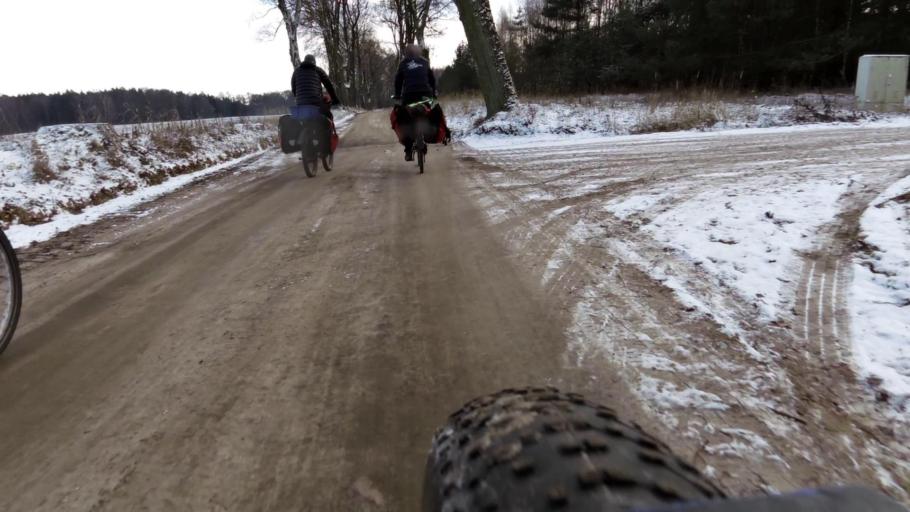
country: PL
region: West Pomeranian Voivodeship
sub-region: Powiat walecki
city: Walcz
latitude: 53.2673
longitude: 16.3110
